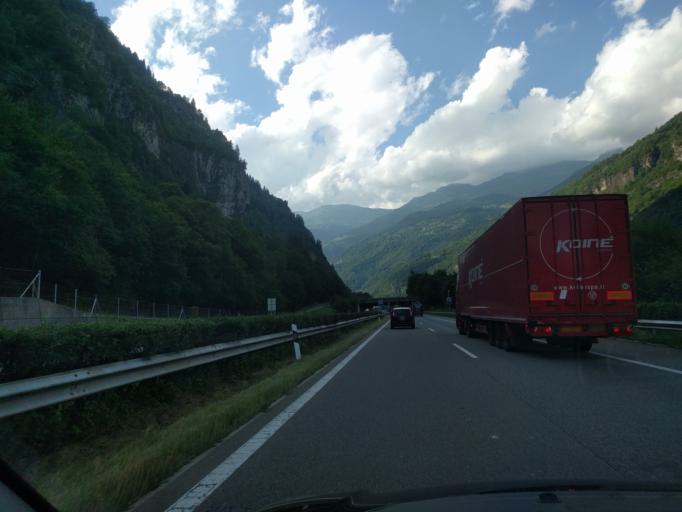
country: CH
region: Ticino
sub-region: Leventina District
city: Faido
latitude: 46.4503
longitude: 8.8292
